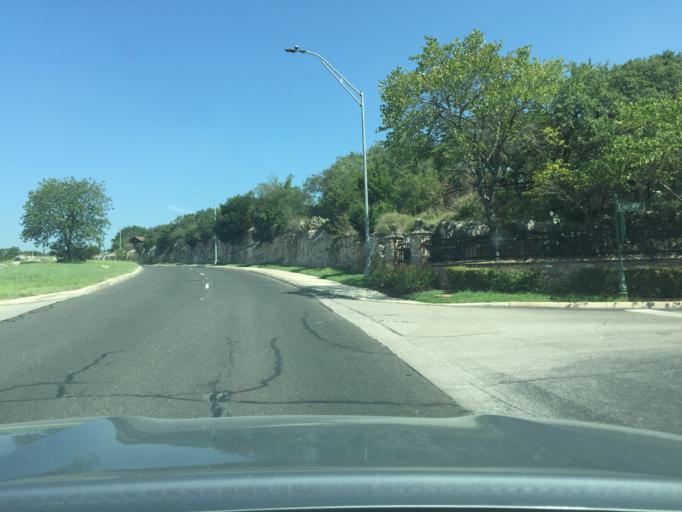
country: US
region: Texas
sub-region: Bexar County
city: Timberwood Park
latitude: 29.6600
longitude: -98.4977
